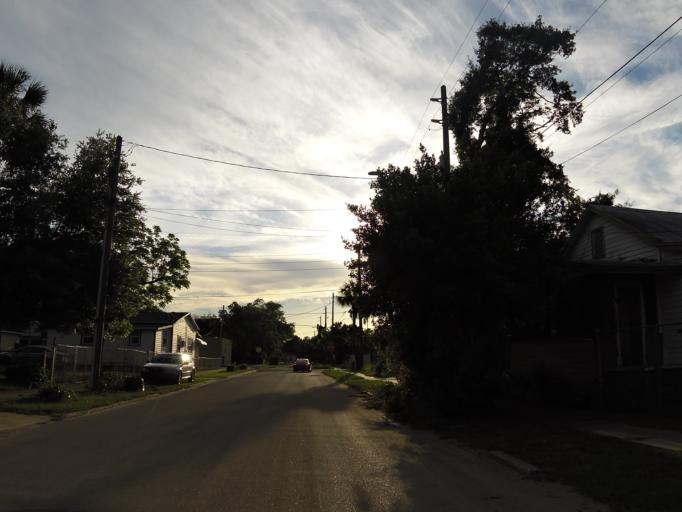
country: US
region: Florida
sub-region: Duval County
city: Jacksonville
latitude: 30.3402
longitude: -81.6415
